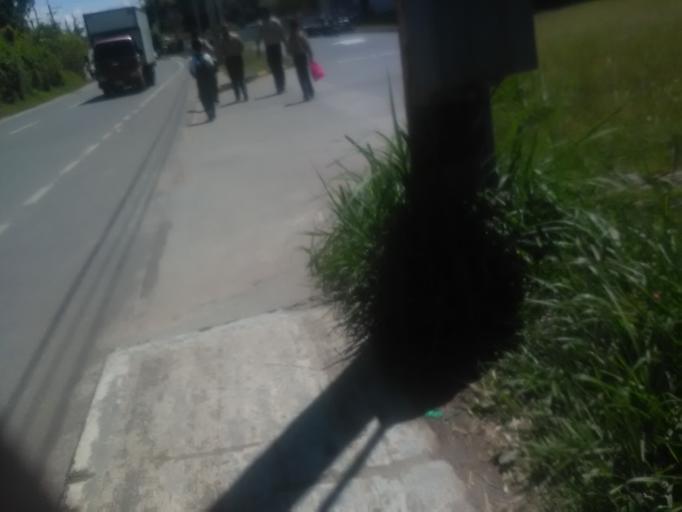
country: CO
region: Antioquia
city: Rionegro
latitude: 6.1419
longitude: -75.3804
